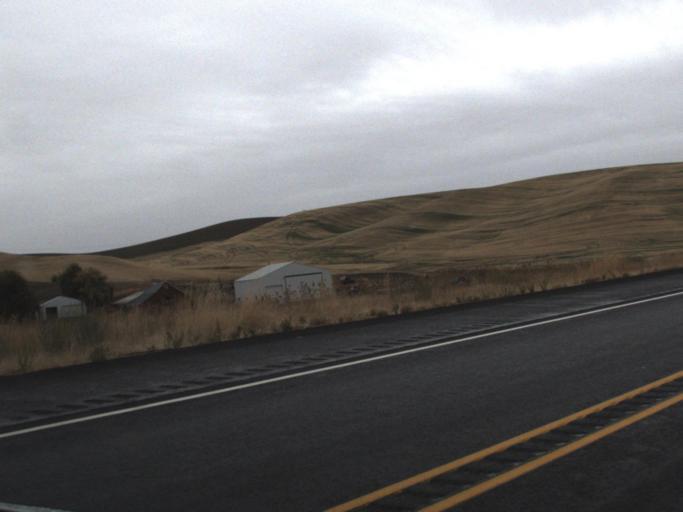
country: US
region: Washington
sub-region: Whitman County
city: Colfax
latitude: 46.8375
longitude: -117.3380
